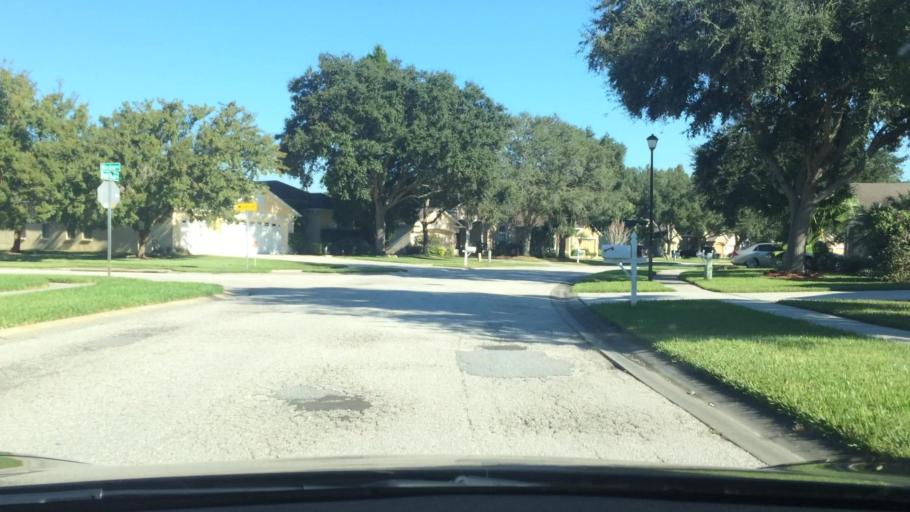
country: US
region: Florida
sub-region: Pasco County
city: Land O' Lakes
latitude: 28.2080
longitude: -82.4010
